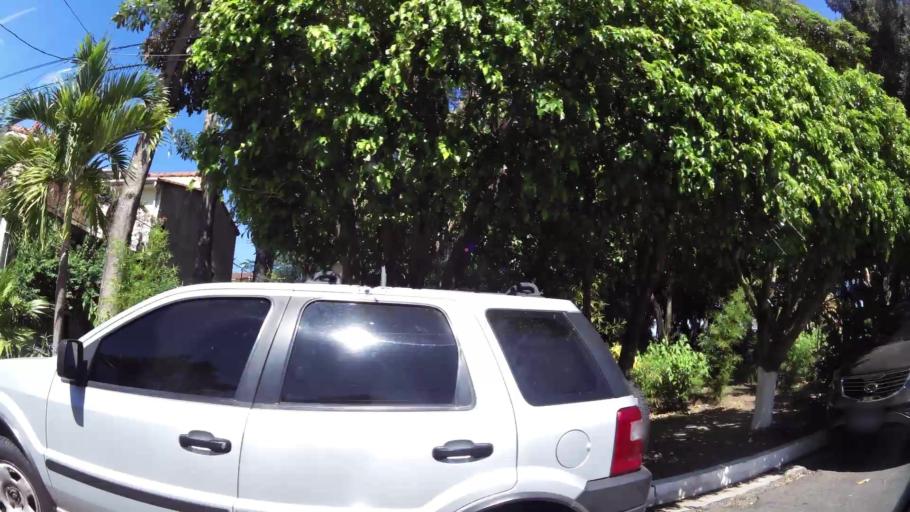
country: SV
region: La Libertad
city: Santa Tecla
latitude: 13.6661
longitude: -89.2786
